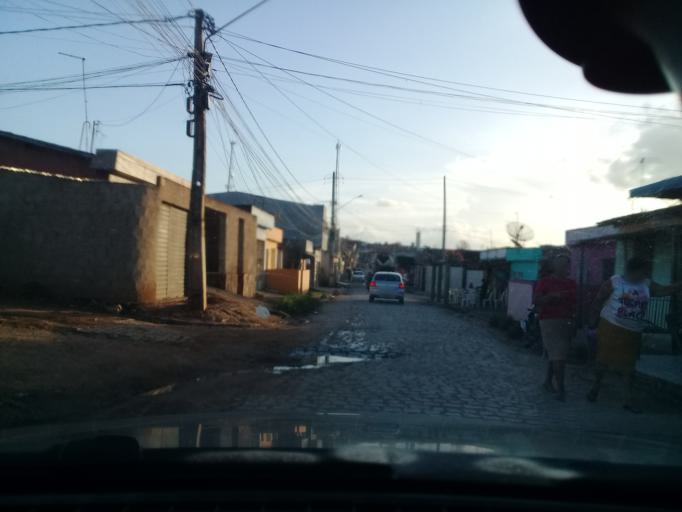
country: BR
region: Pernambuco
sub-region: Vitoria De Santo Antao
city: Vitoria de Santo Antao
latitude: -8.1279
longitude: -35.2849
